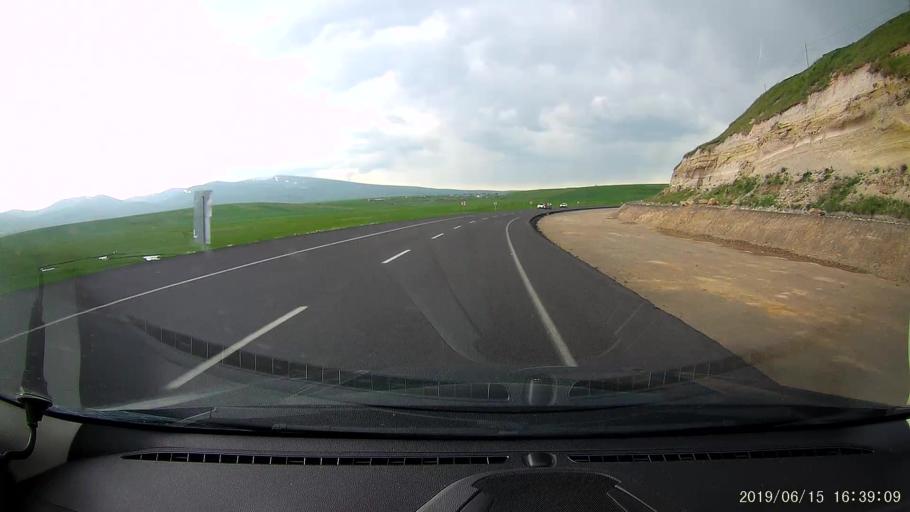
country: TR
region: Ardahan
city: Haskoy
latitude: 40.9859
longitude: 42.8946
